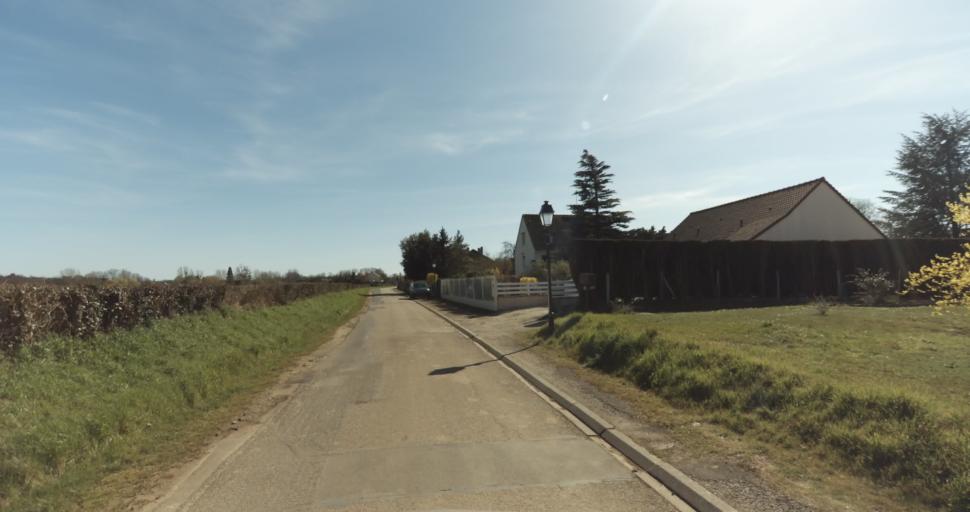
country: FR
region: Lower Normandy
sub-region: Departement du Calvados
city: Saint-Pierre-sur-Dives
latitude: 49.0439
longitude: -0.0264
